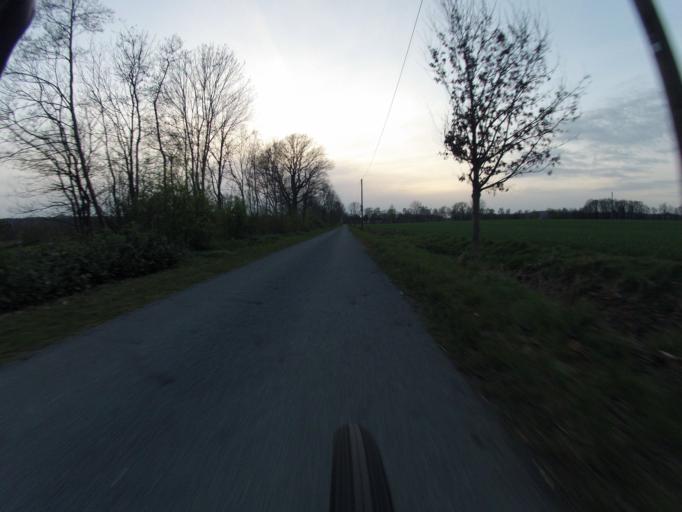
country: DE
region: North Rhine-Westphalia
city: Ibbenburen
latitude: 52.2502
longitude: 7.7621
